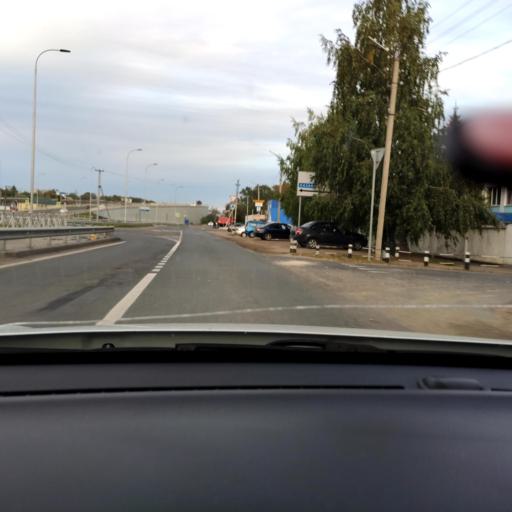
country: RU
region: Tatarstan
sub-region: Zelenodol'skiy Rayon
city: Zelenodolsk
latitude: 55.8396
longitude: 48.5395
